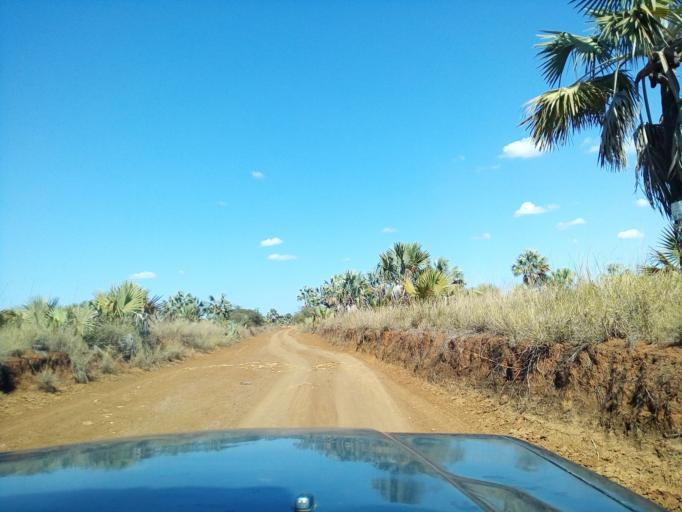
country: MG
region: Boeny
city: Mahajanga
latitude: -15.8694
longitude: 46.1396
